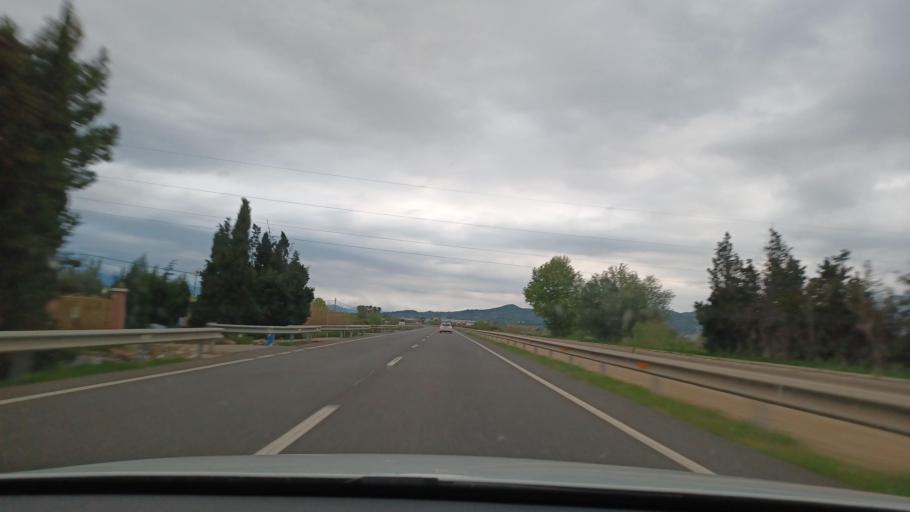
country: ES
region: Catalonia
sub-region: Provincia de Tarragona
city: Amposta
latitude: 40.7313
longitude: 0.5699
